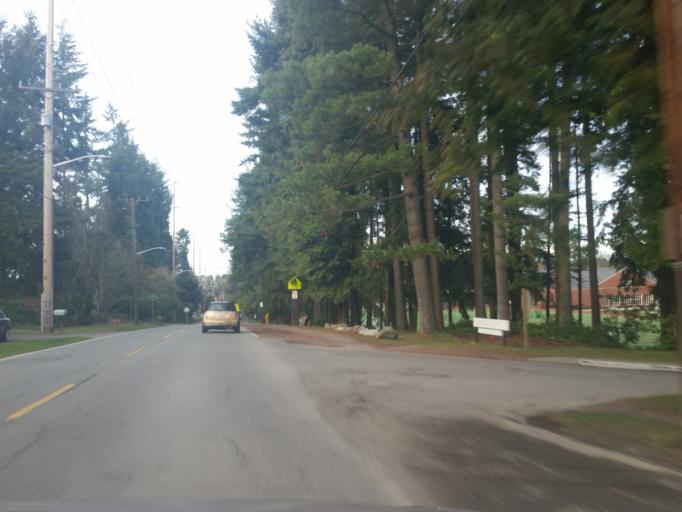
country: US
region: Washington
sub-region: King County
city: Shoreline
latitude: 47.7315
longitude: -122.3289
